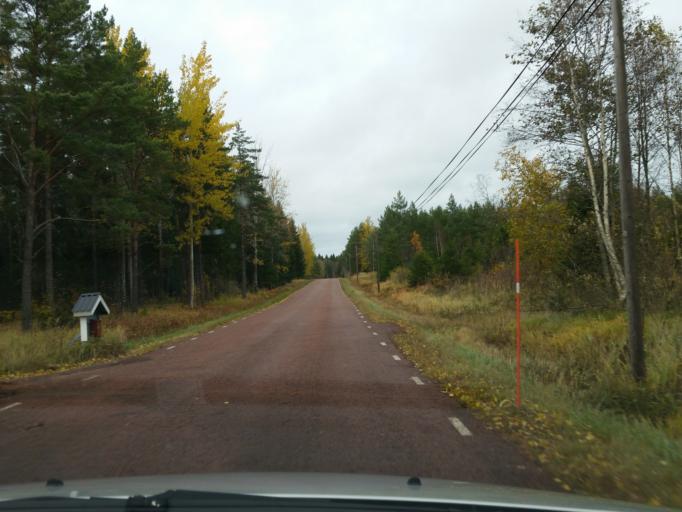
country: AX
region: Alands landsbygd
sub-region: Lemland
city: Lemland
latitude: 60.0038
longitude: 20.1869
